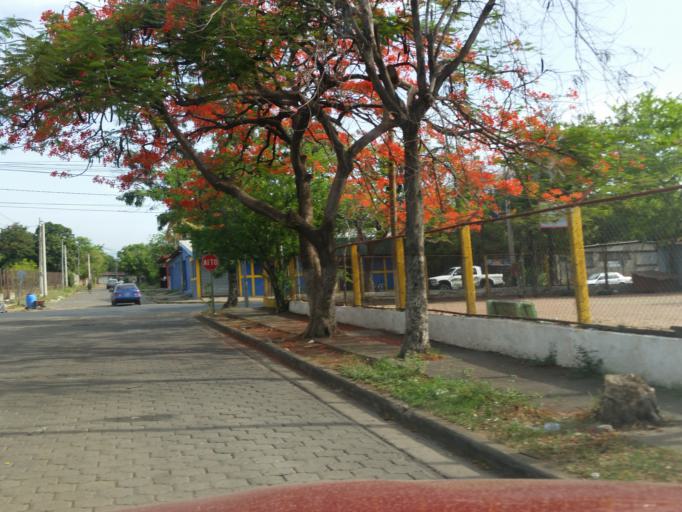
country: NI
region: Managua
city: Managua
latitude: 12.1387
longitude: -86.2641
